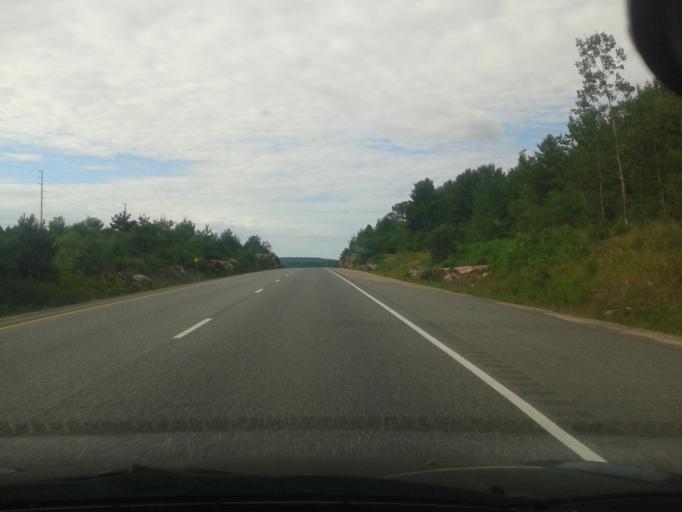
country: CA
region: Ontario
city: Powassan
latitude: 46.1065
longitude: -79.3669
